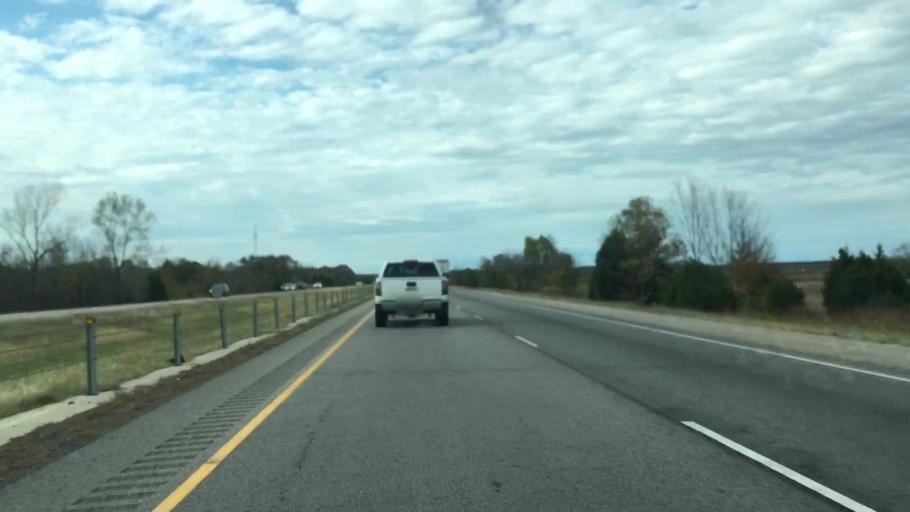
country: US
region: Arkansas
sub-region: Conway County
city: Morrilton
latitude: 35.1976
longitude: -92.8025
